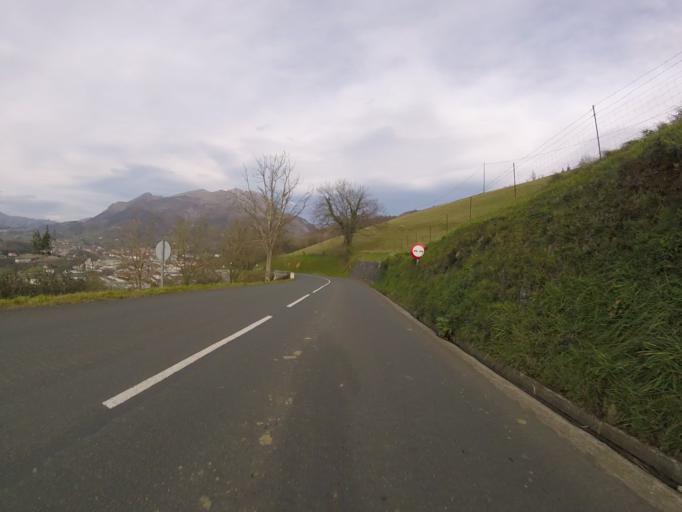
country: ES
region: Basque Country
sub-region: Provincia de Guipuzcoa
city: Azpeitia
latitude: 43.1711
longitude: -2.2458
